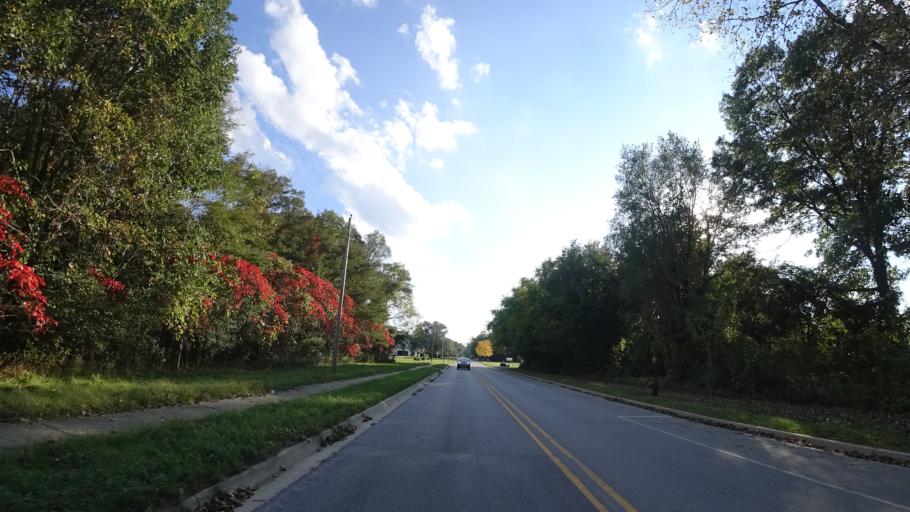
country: US
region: Michigan
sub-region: Saint Joseph County
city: Three Rivers
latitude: 41.9598
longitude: -85.6247
